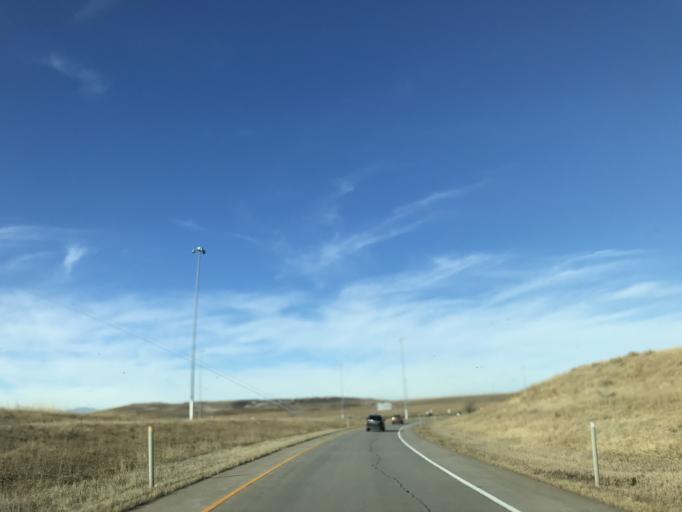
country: US
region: Colorado
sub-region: Adams County
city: Aurora
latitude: 39.8376
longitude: -104.7454
